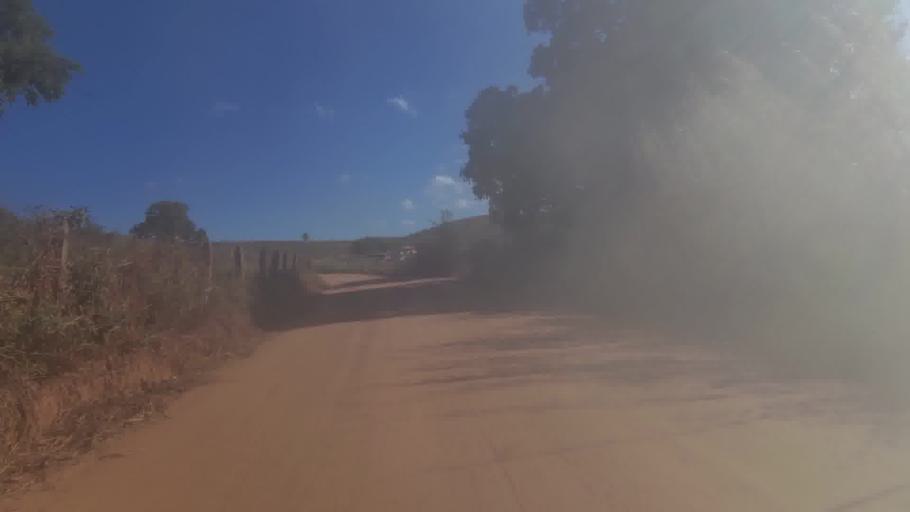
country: BR
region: Espirito Santo
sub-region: Cachoeiro De Itapemirim
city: Cachoeiro de Itapemirim
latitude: -21.0230
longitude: -41.0515
